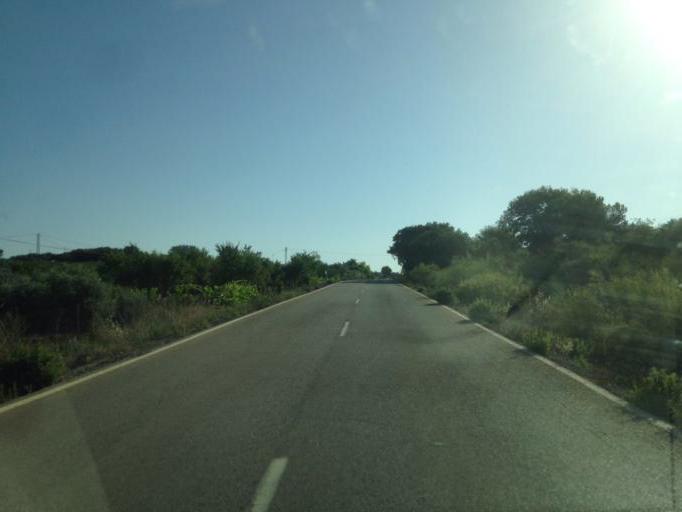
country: ES
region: Andalusia
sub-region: Provincia de Malaga
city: Archidona
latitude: 37.1076
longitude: -4.3488
